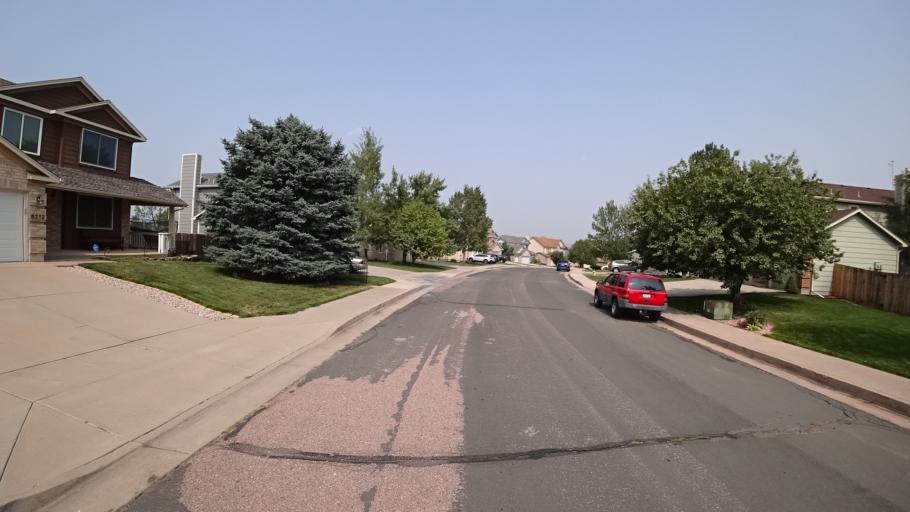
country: US
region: Colorado
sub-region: El Paso County
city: Cimarron Hills
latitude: 38.9196
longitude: -104.7487
